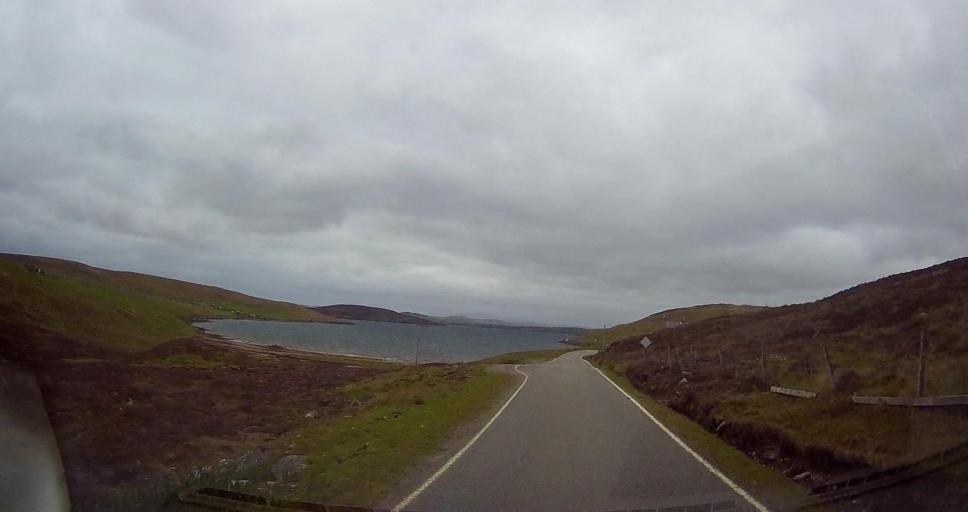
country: GB
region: Scotland
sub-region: Shetland Islands
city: Lerwick
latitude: 60.3315
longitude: -1.3350
